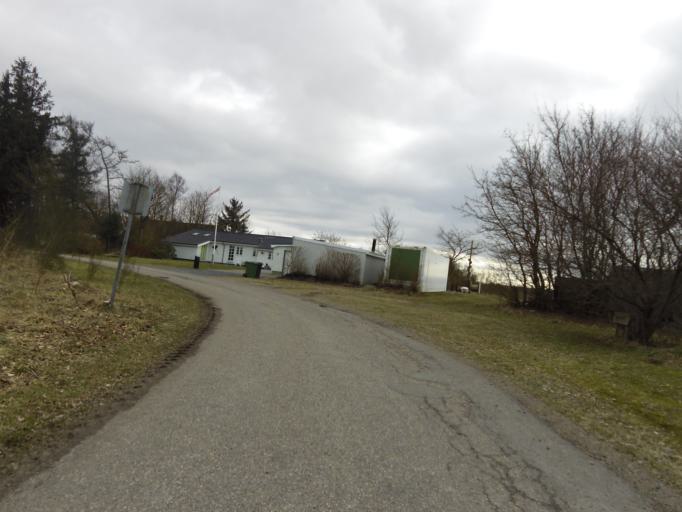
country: DK
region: South Denmark
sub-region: Tonder Kommune
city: Toftlund
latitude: 55.2093
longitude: 9.1736
